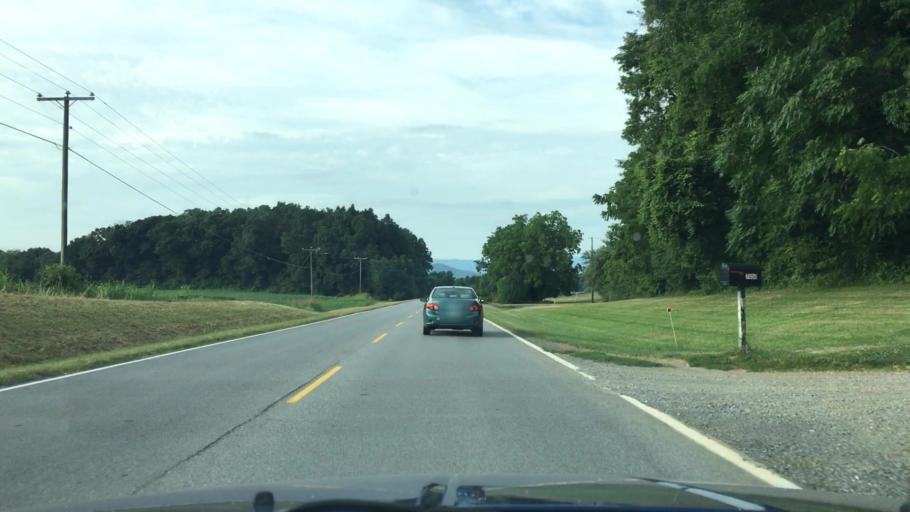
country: US
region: Virginia
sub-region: City of Waynesboro
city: Waynesboro
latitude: 38.0964
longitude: -78.8987
